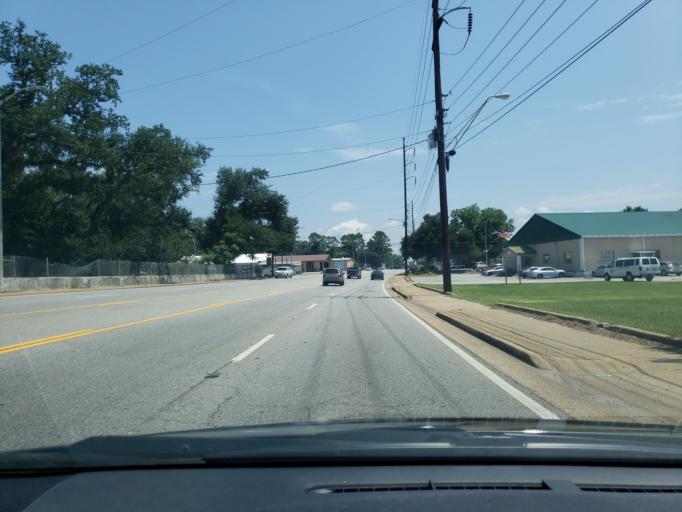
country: US
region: Georgia
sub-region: Dougherty County
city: Albany
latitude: 31.5812
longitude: -84.1882
